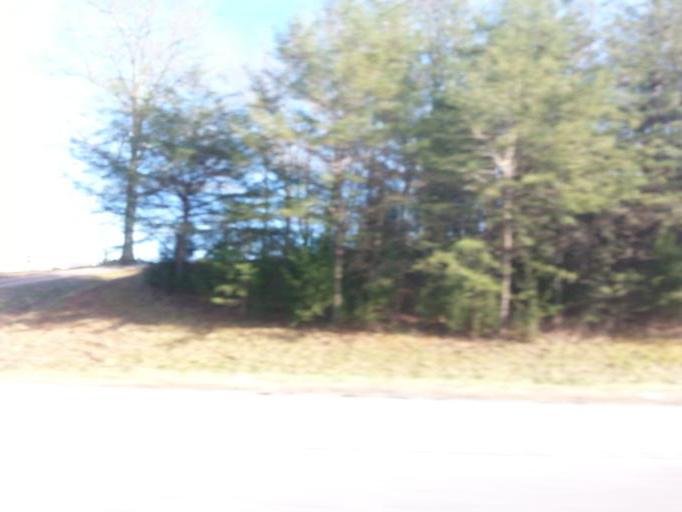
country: US
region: Tennessee
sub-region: Van Buren County
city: Spencer
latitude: 35.7988
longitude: -85.5765
